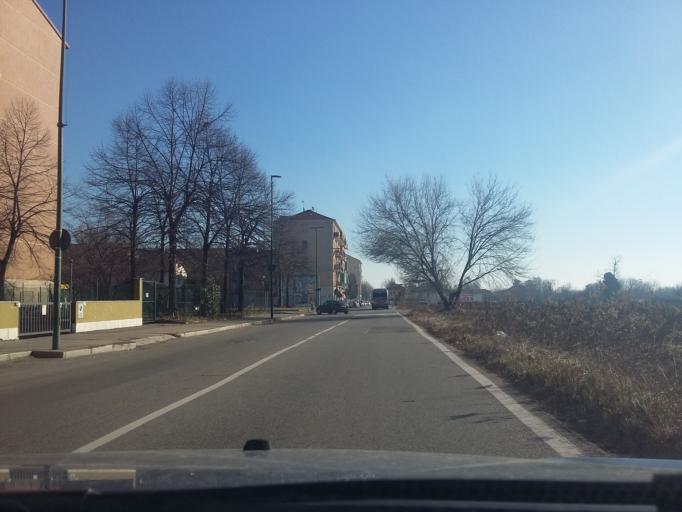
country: IT
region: Piedmont
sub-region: Provincia di Torino
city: Nichelino
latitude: 45.0115
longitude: 7.6319
